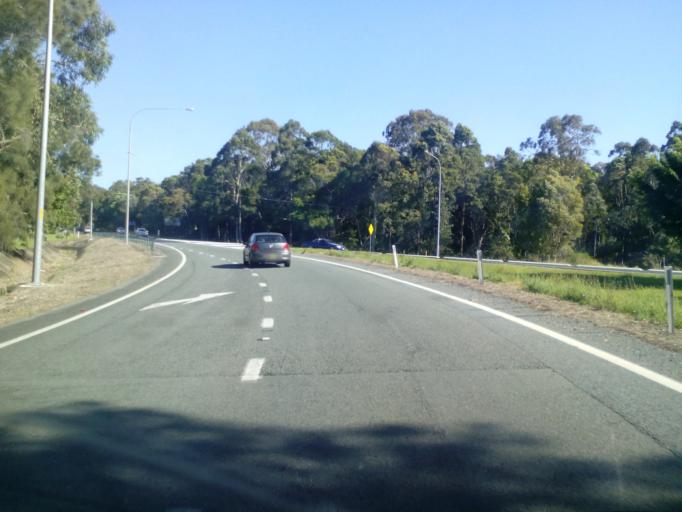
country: AU
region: New South Wales
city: Chinderah
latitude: -28.2449
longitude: 153.5539
